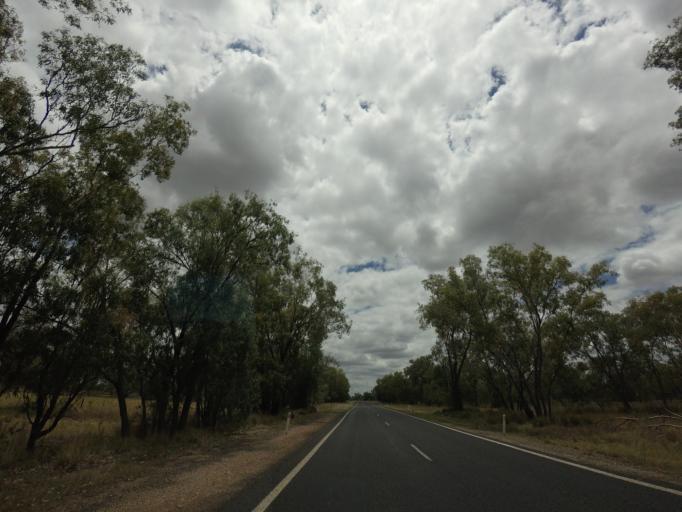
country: AU
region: Queensland
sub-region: Goondiwindi
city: Goondiwindi
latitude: -28.4851
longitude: 150.2934
